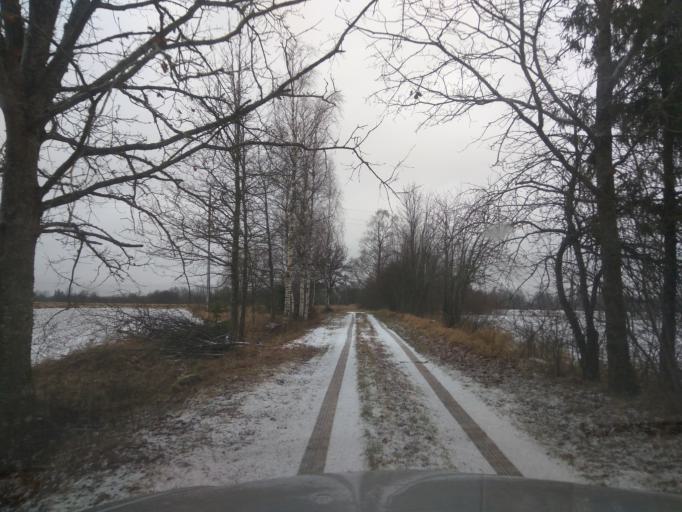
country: LV
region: Broceni
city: Broceni
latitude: 56.8482
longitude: 22.3882
